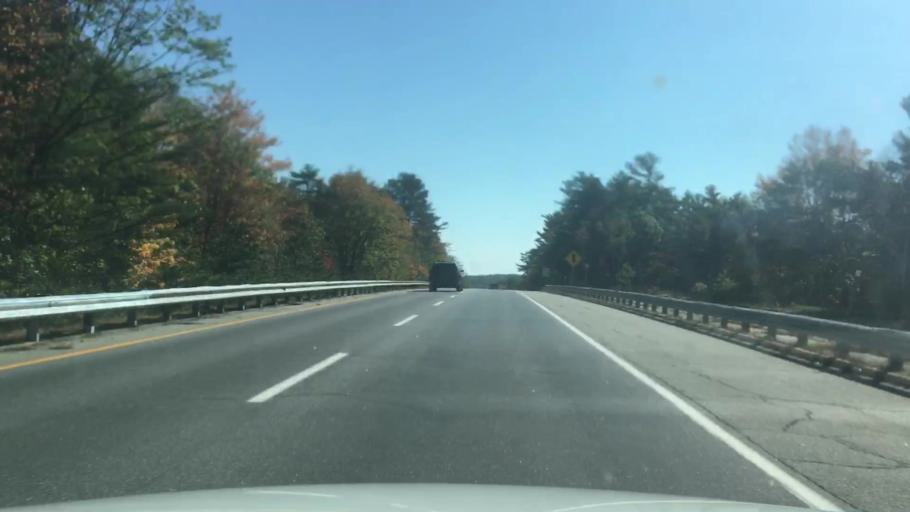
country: US
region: Maine
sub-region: Sagadahoc County
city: Bath
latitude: 43.9103
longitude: -69.8445
